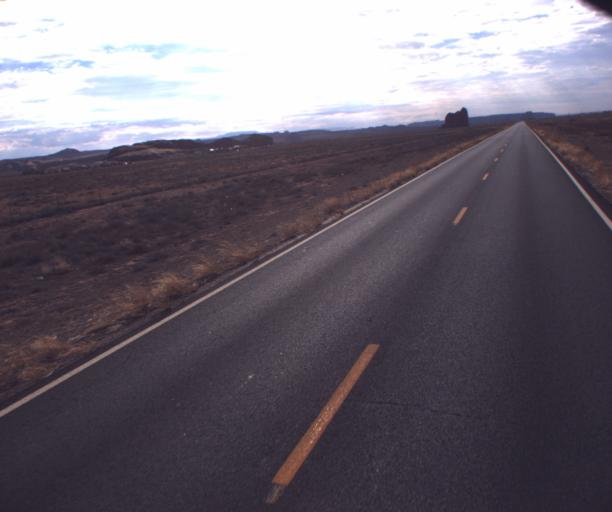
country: US
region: Arizona
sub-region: Apache County
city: Many Farms
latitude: 36.7561
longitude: -109.6470
